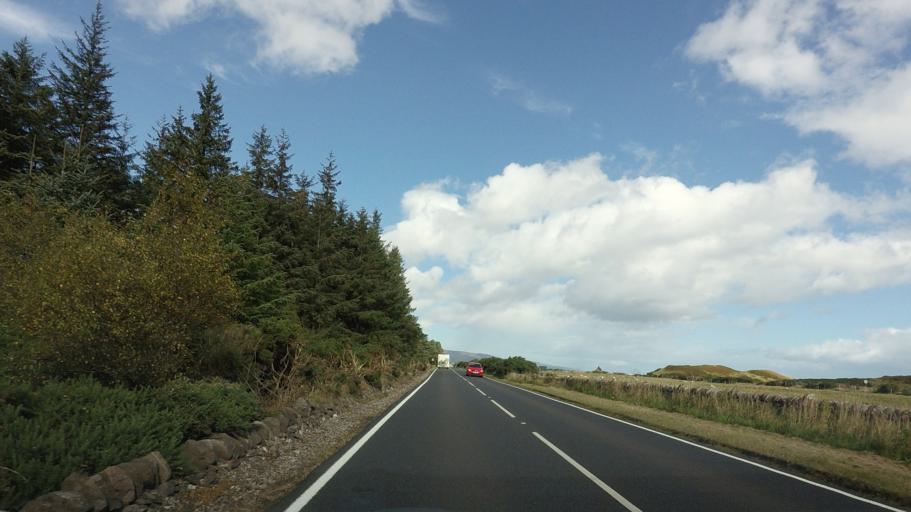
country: GB
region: Scotland
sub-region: Highland
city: Brora
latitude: 57.9932
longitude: -3.8923
